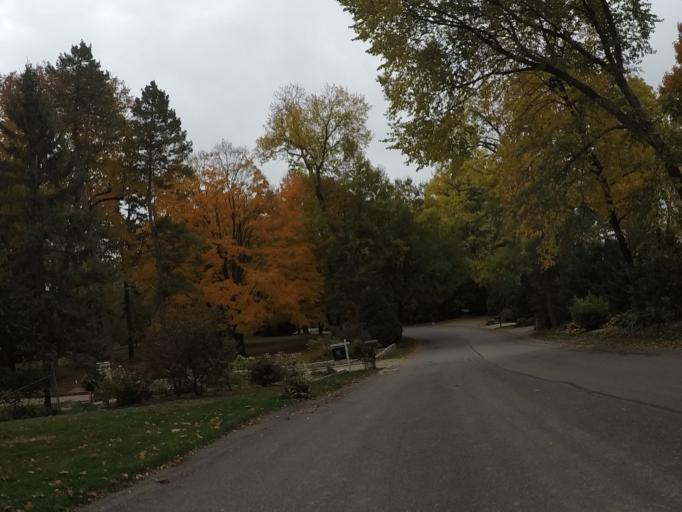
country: US
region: Wisconsin
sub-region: Dane County
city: Maple Bluff
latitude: 43.1146
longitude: -89.3779
